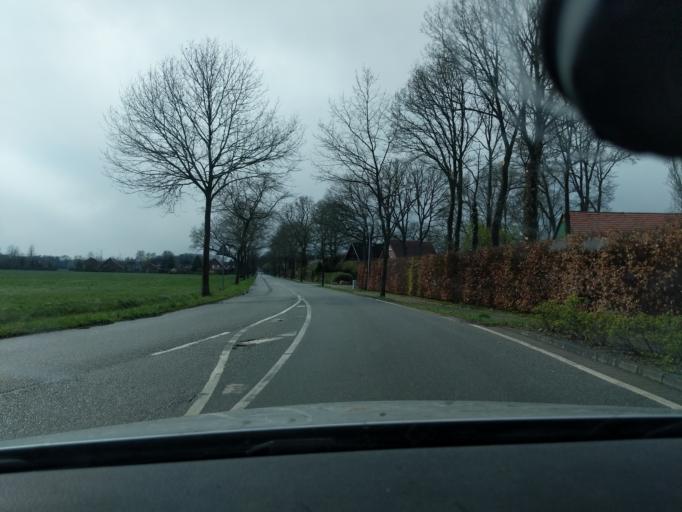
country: DE
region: Lower Saxony
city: Ahlerstedt
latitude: 53.4022
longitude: 9.4640
